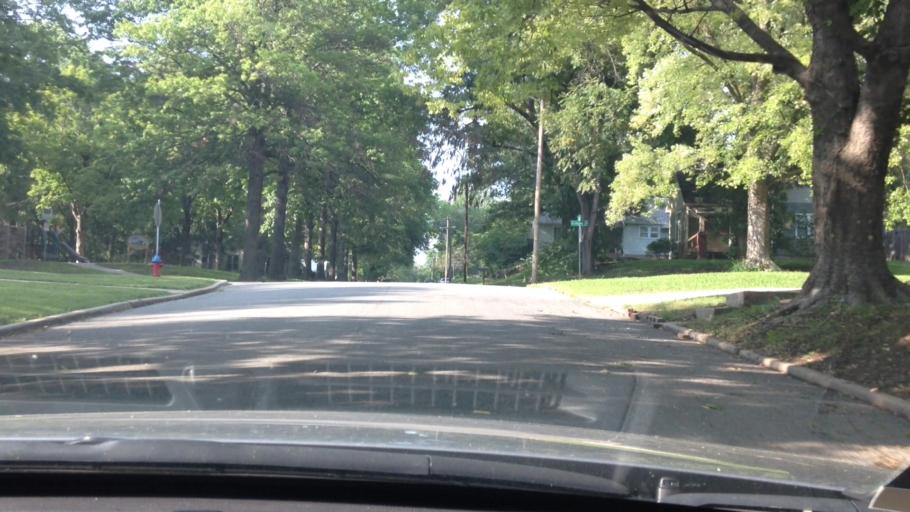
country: US
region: Kansas
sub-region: Leavenworth County
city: Leavenworth
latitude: 39.3228
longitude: -94.9304
